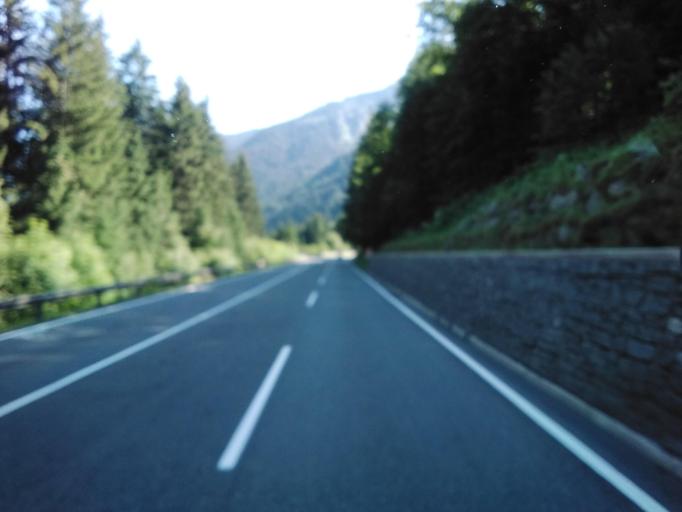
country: AT
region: Salzburg
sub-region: Politischer Bezirk Zell am See
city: Mittersill
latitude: 47.2221
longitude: 12.4887
